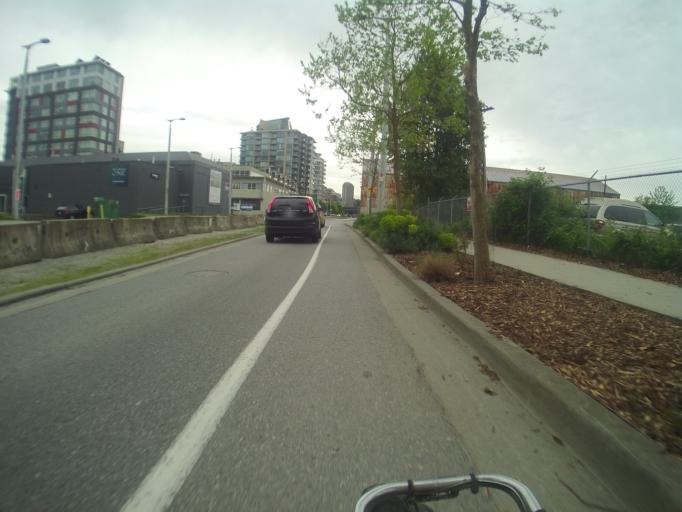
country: CA
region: British Columbia
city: Vancouver
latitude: 49.2702
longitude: -123.1103
